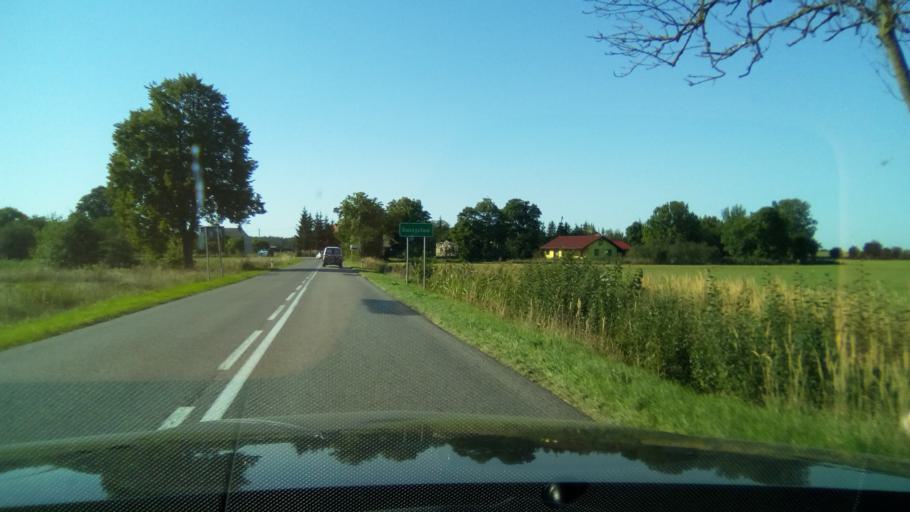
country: PL
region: West Pomeranian Voivodeship
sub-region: Powiat kamienski
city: Golczewo
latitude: 53.8333
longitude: 14.8837
